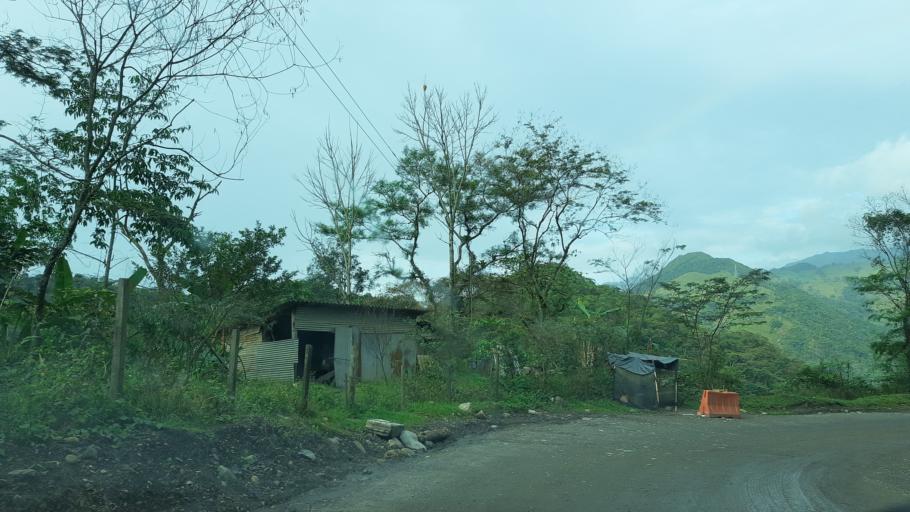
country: CO
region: Boyaca
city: Santa Maria
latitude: 4.8737
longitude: -73.2389
